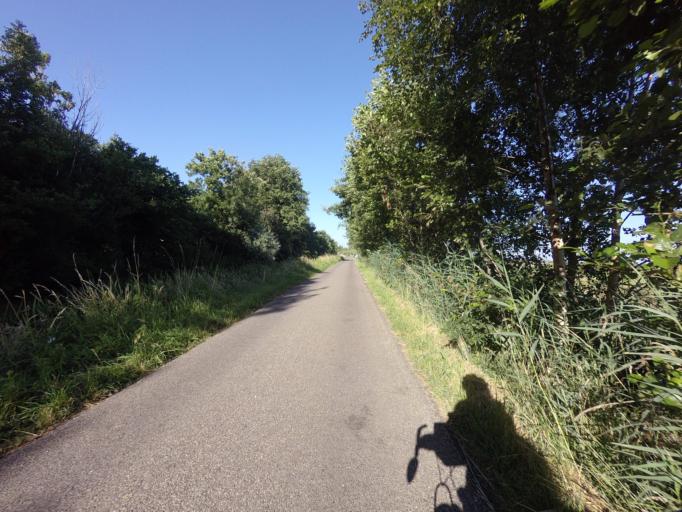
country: NL
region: South Holland
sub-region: Gemeente Vlist
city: Haastrecht
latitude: 52.0192
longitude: 4.7550
